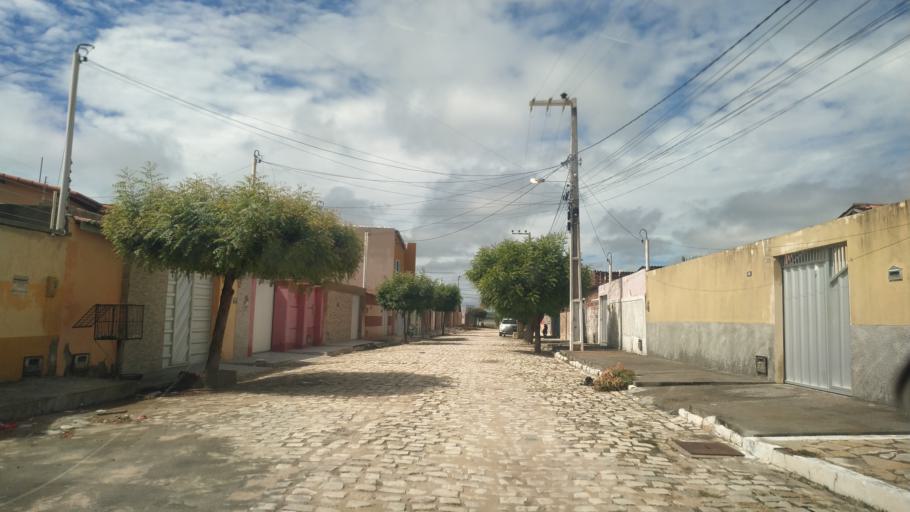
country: BR
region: Rio Grande do Norte
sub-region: Areia Branca
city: Areia Branca
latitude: -4.9532
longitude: -37.1238
